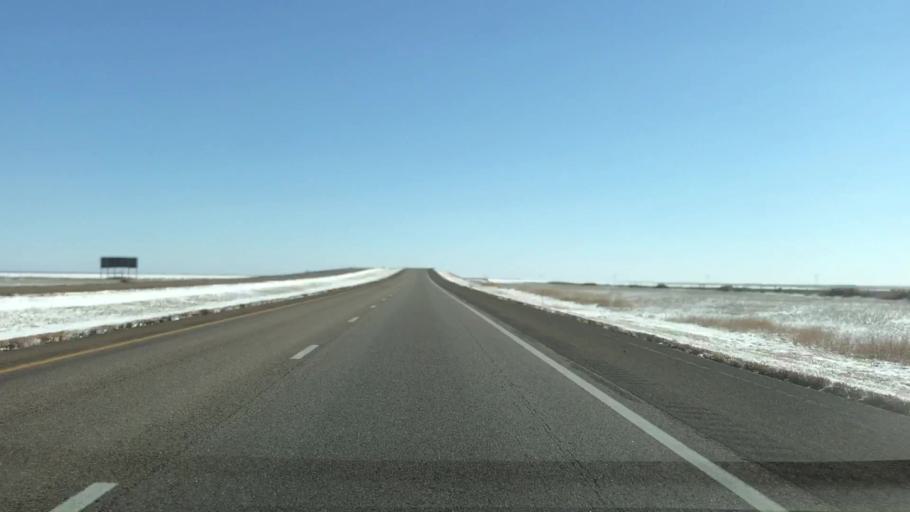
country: US
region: Kansas
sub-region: Thomas County
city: Colby
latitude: 39.3156
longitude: -100.9843
